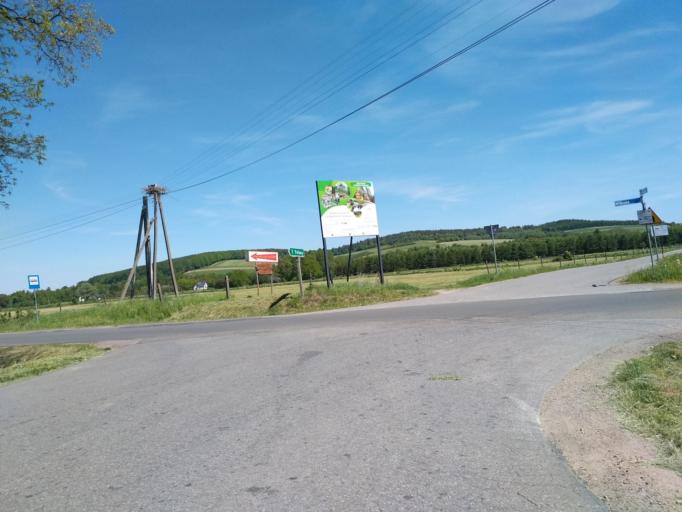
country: PL
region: Subcarpathian Voivodeship
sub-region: Powiat krosnienski
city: Sieniawa
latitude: 49.5508
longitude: 21.9406
